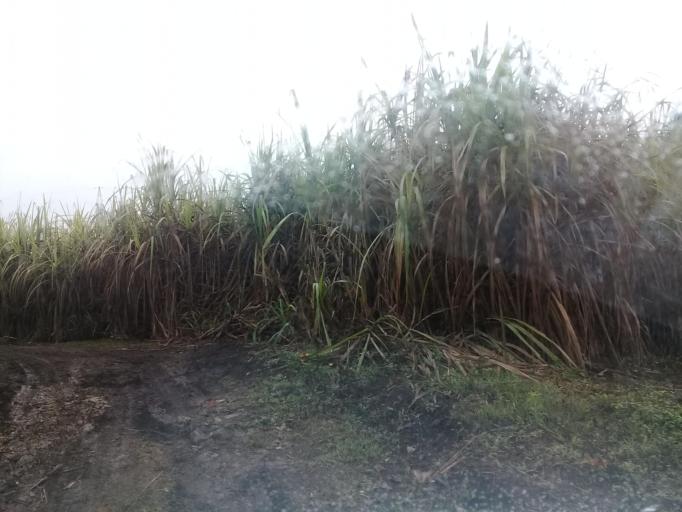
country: MX
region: Veracruz
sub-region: Amatlan de los Reyes
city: Centro de Readaptacion Social
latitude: 18.8190
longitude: -96.9445
